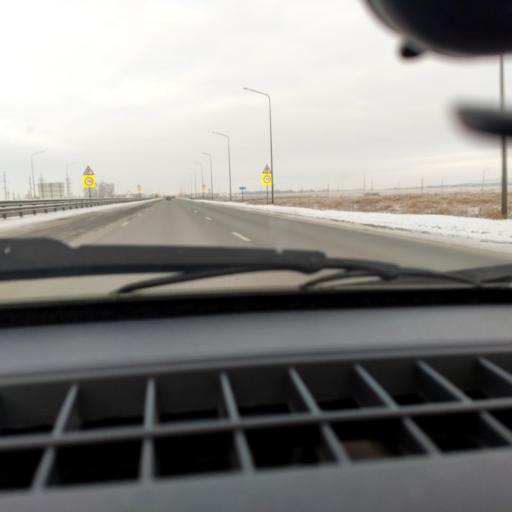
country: RU
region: Bashkortostan
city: Asanovo
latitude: 54.8963
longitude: 55.6382
